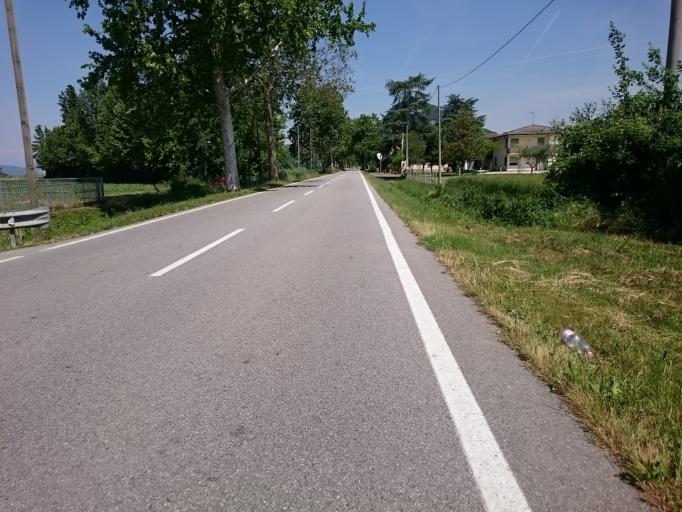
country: IT
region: Veneto
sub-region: Provincia di Padova
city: Lozzo Atestino
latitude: 45.2676
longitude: 11.6164
